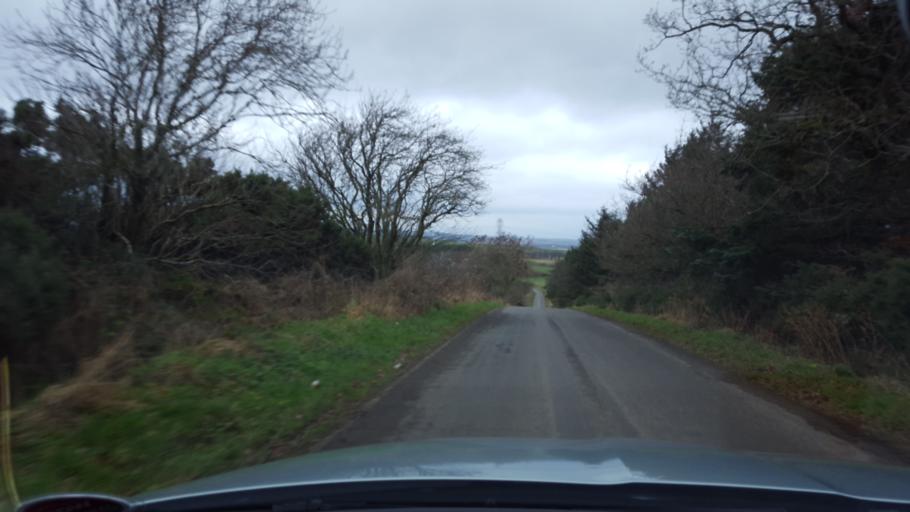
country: GB
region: Scotland
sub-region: West Lothian
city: Kirknewton
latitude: 55.8672
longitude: -3.4331
